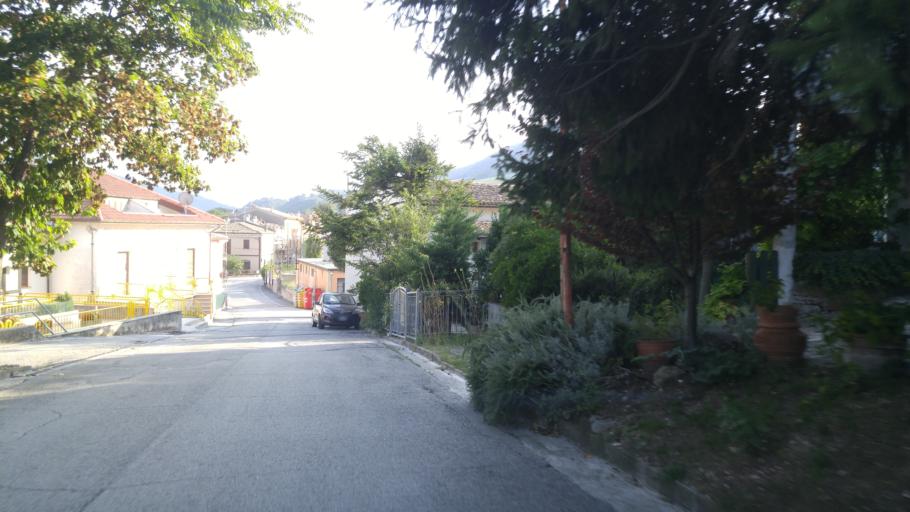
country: IT
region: The Marches
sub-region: Provincia di Pesaro e Urbino
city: Acqualagna
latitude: 43.6184
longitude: 12.6711
